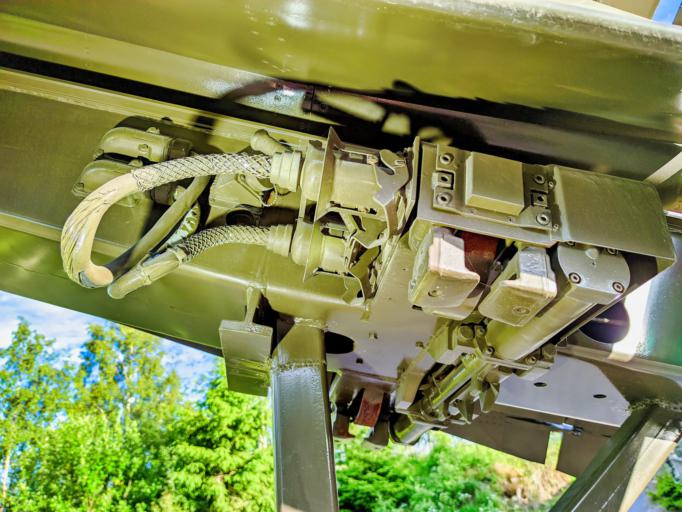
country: NO
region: Ostfold
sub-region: Trogstad
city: Skjonhaug
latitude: 59.6340
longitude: 11.3410
